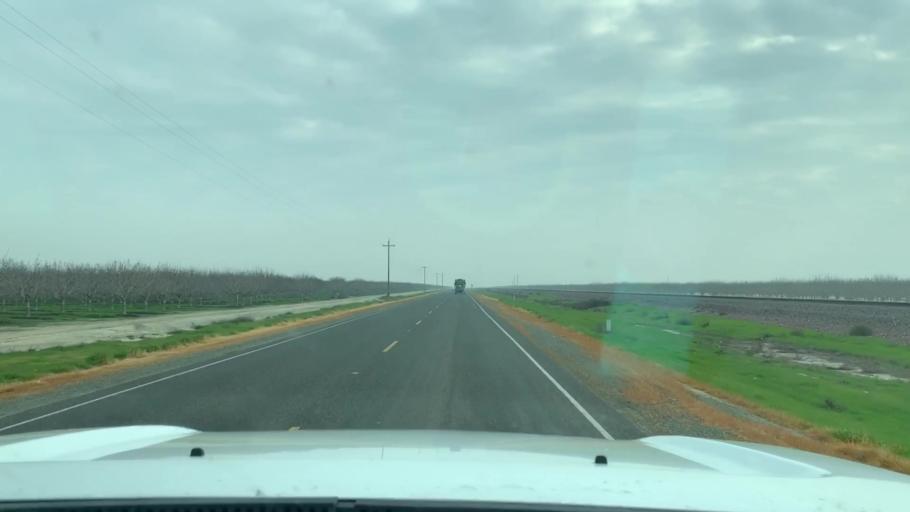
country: US
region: California
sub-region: Tulare County
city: Earlimart
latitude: 35.8245
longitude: -119.3670
